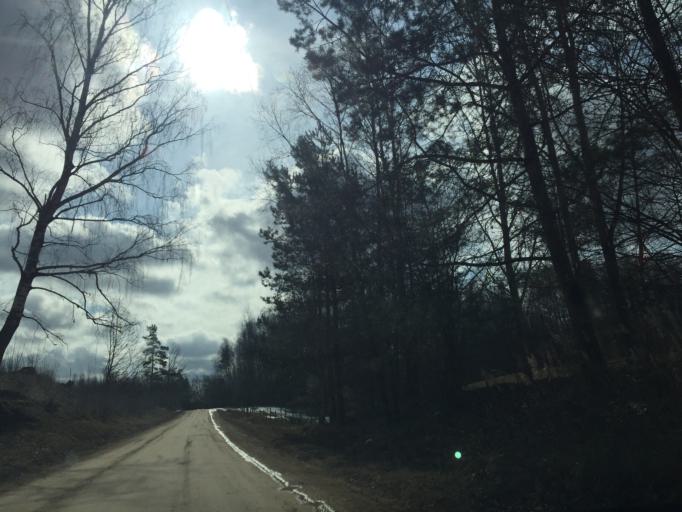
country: LV
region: Vecumnieki
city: Vecumnieki
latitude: 56.5878
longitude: 24.5609
